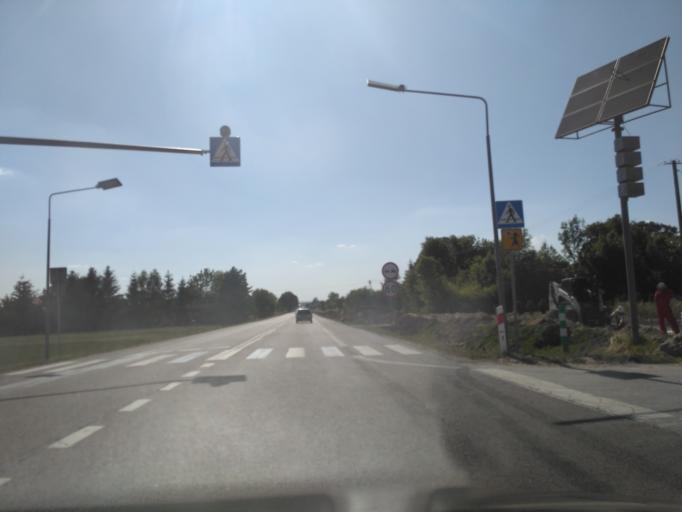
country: PL
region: Lublin Voivodeship
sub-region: Powiat swidnicki
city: Trawniki
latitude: 51.1669
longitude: 23.0706
